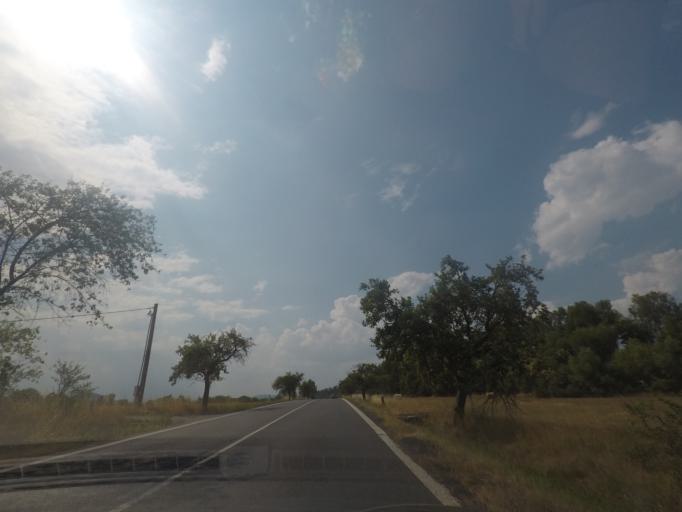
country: CZ
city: Brniste
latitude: 50.7726
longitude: 14.7006
